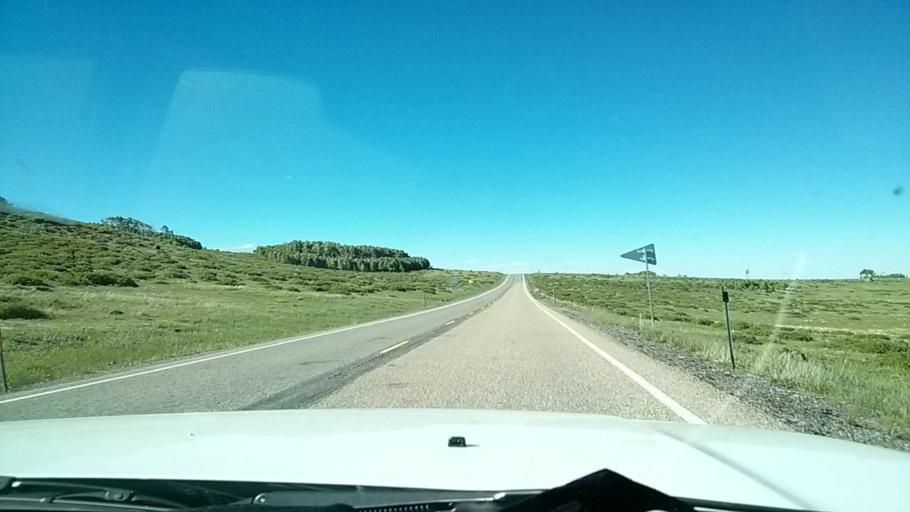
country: US
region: Utah
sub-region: Wayne County
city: Loa
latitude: 38.0382
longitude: -111.3297
